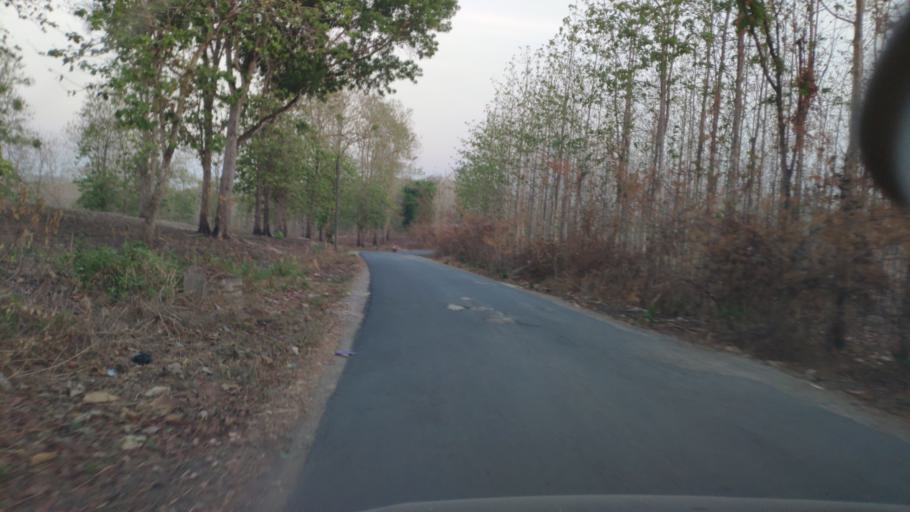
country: ID
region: Central Java
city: Ngliron
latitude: -7.0915
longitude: 111.4234
